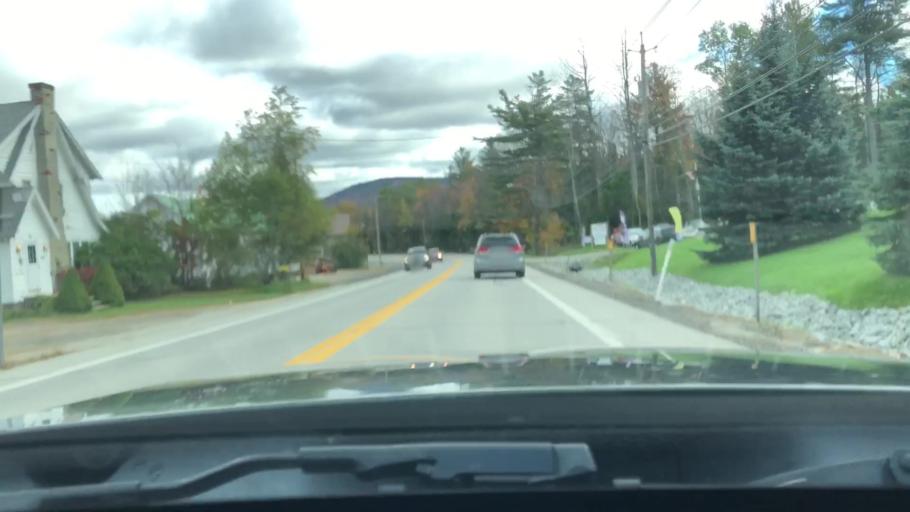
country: US
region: New York
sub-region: Hamilton County
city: Lake Pleasant
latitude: 43.4703
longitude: -74.4091
